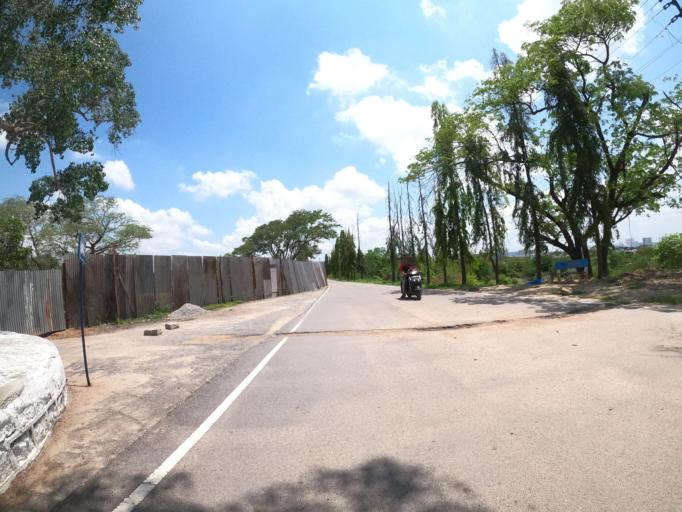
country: IN
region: Telangana
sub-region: Medak
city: Serilingampalle
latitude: 17.3818
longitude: 78.3169
